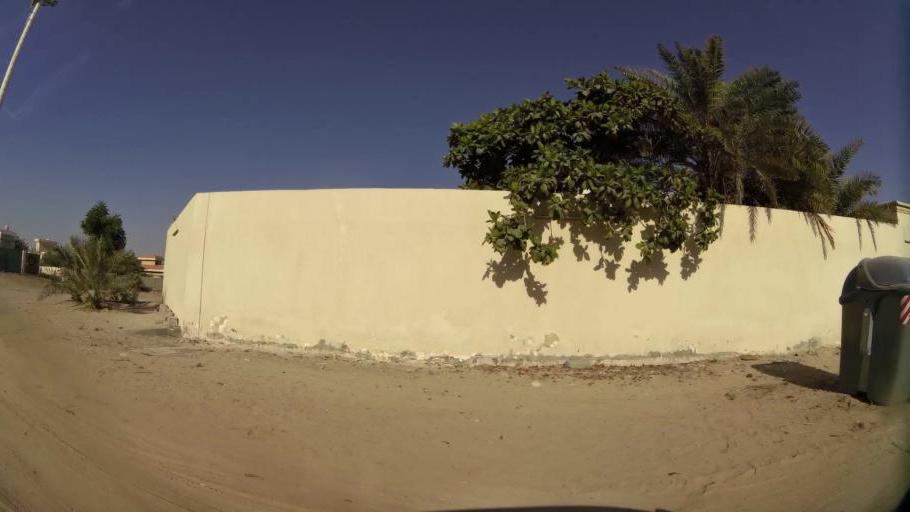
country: AE
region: Ajman
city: Ajman
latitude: 25.4030
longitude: 55.4608
